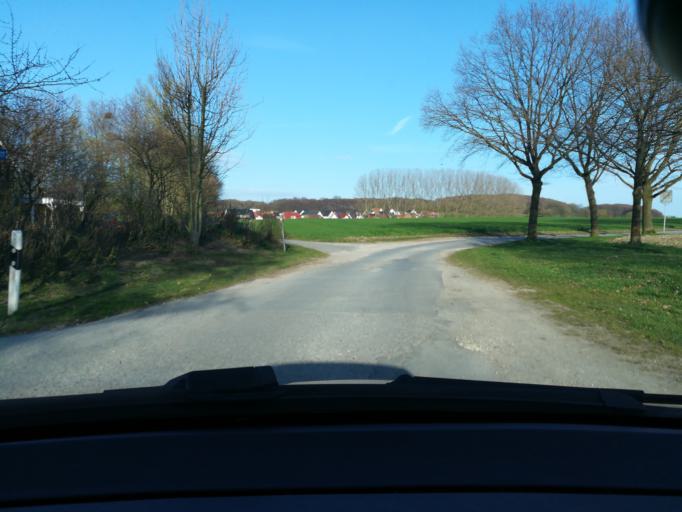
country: DE
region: North Rhine-Westphalia
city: Borgholzhausen
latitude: 52.0957
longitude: 8.2982
